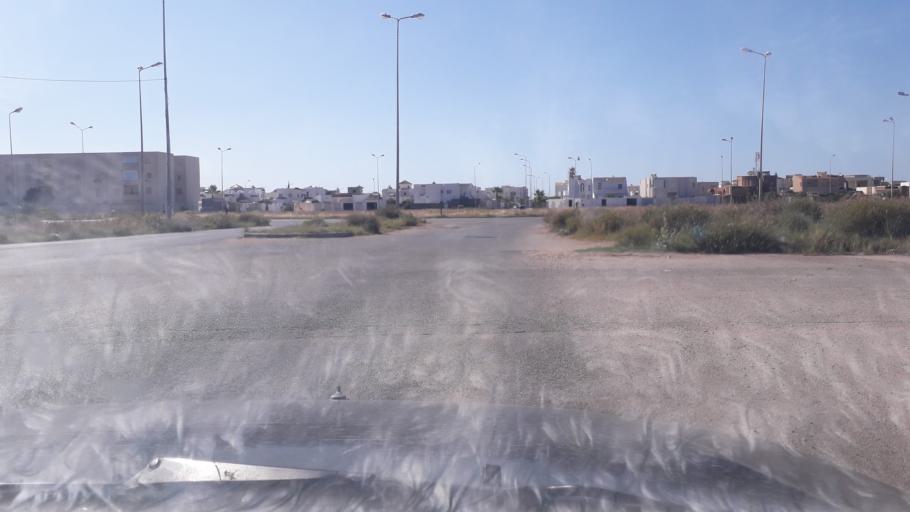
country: TN
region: Safaqis
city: Al Qarmadah
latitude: 34.8324
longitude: 10.7552
